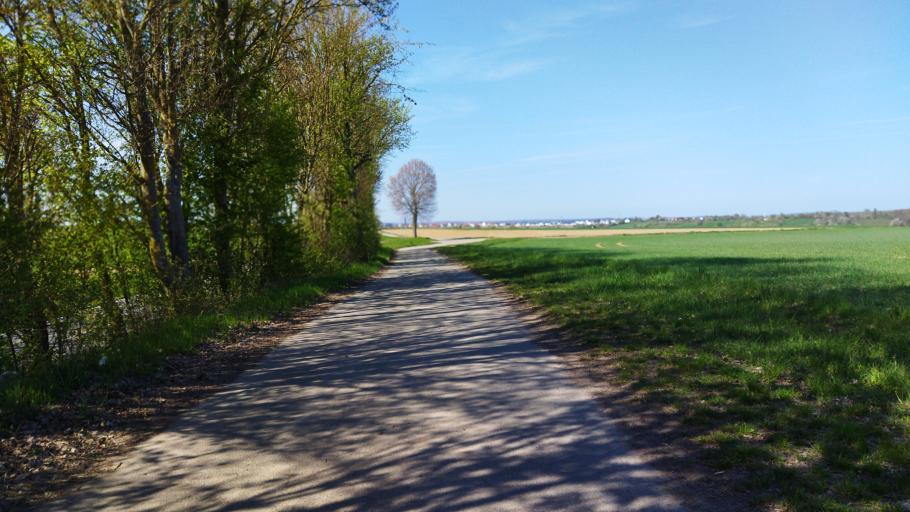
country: DE
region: Baden-Wuerttemberg
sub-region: Regierungsbezirk Stuttgart
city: Bad Wimpfen
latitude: 49.2058
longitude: 9.1490
